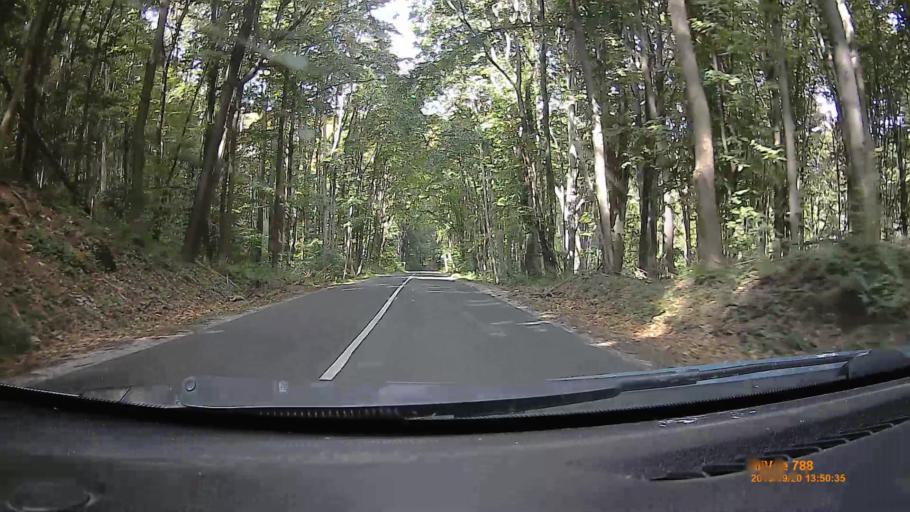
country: HU
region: Borsod-Abauj-Zemplen
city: Saly
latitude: 48.0682
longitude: 20.5896
